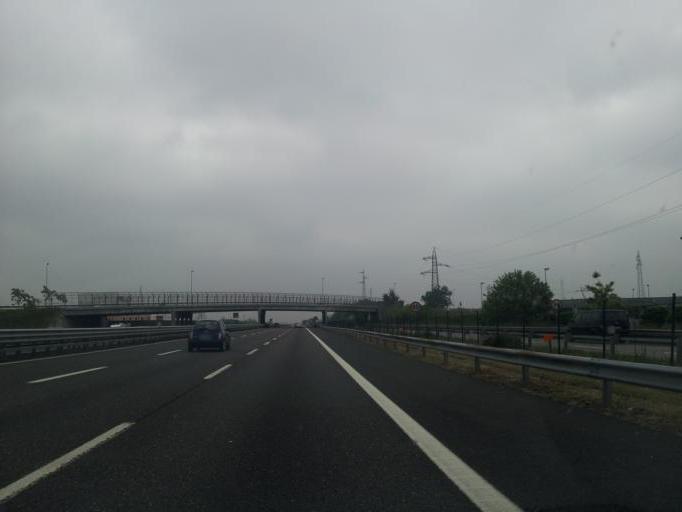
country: IT
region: Veneto
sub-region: Provincia di Verona
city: San Giovanni Lupatoto
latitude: 45.4003
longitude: 11.0159
